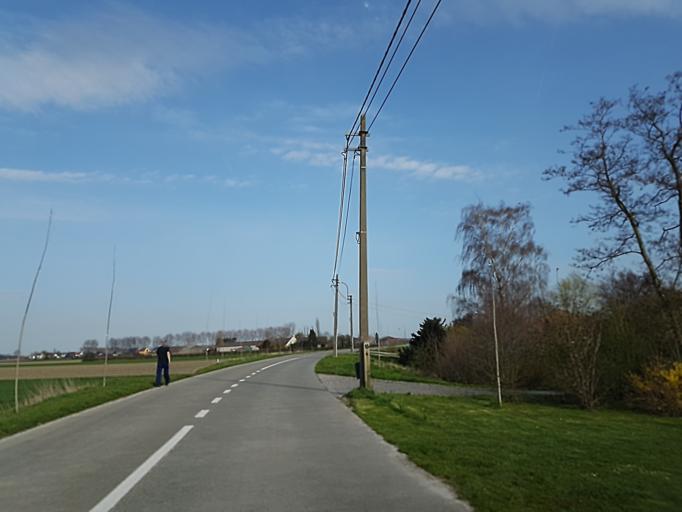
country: BE
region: Flanders
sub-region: Provincie Oost-Vlaanderen
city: Kaprijke
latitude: 51.2771
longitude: 3.6577
